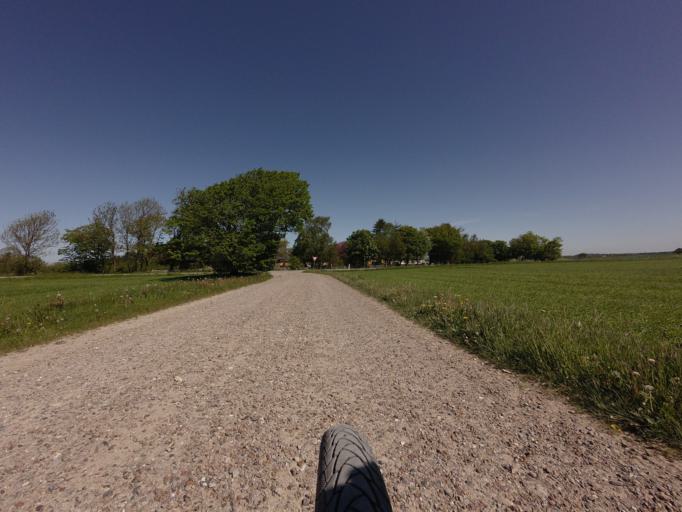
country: DK
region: North Denmark
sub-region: Hjorring Kommune
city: Hjorring
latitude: 57.4517
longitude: 9.8985
